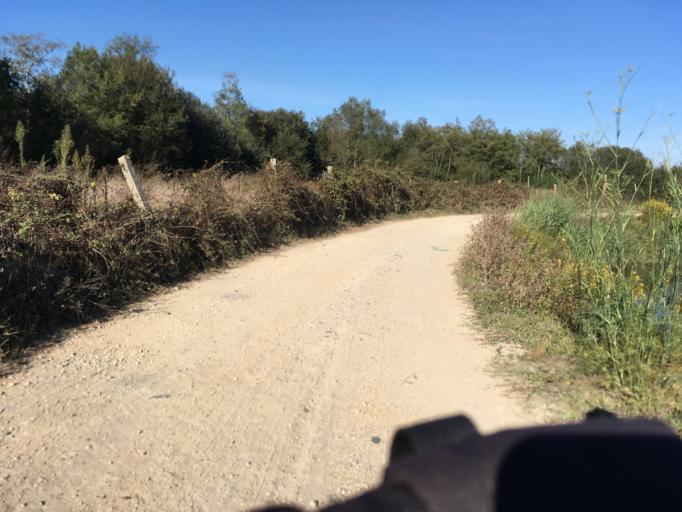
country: PT
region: Aveiro
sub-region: Estarreja
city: Salreu
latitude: 40.7127
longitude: -8.5670
